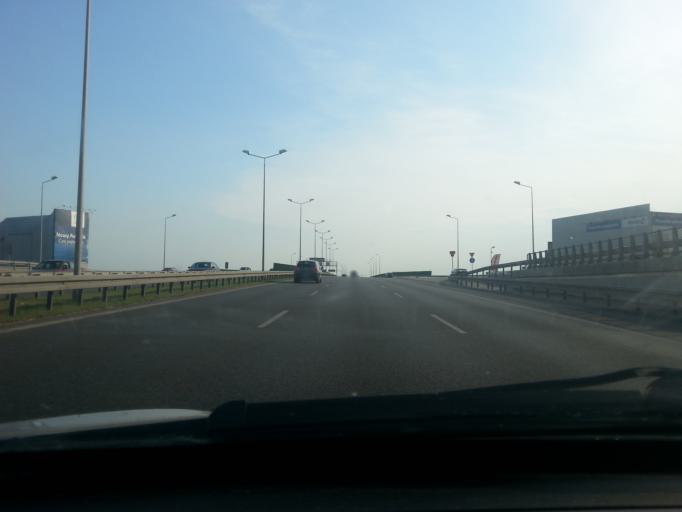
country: PL
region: Masovian Voivodeship
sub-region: Warszawa
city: Bemowo
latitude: 52.2391
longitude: 20.8876
